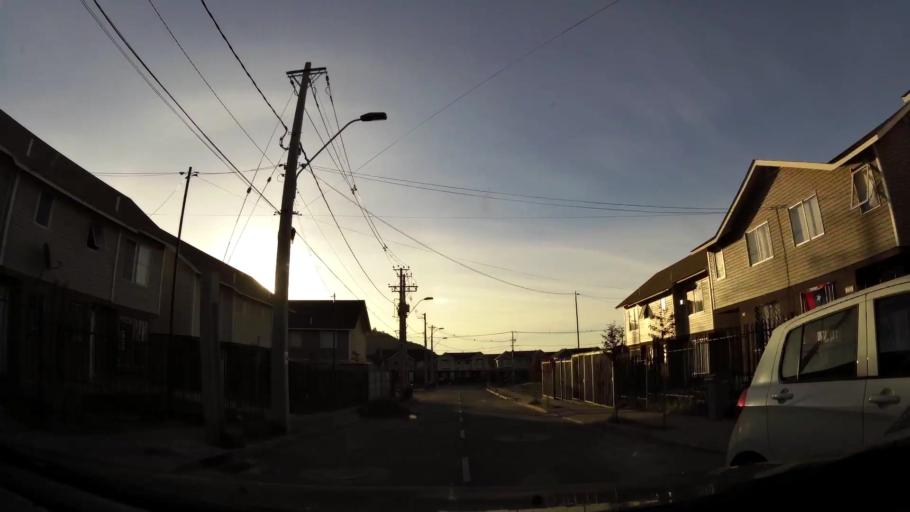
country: CL
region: Santiago Metropolitan
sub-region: Provincia de Cordillera
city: Puente Alto
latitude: -33.6021
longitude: -70.5474
